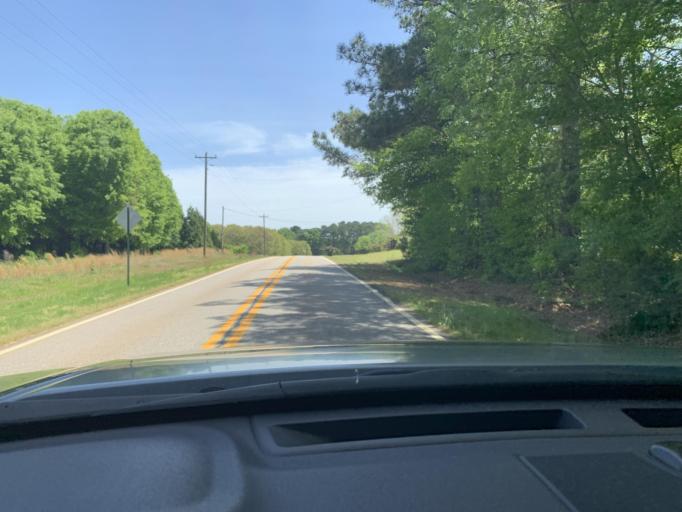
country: US
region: Georgia
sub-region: Oconee County
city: Bogart
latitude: 33.8503
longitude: -83.5394
